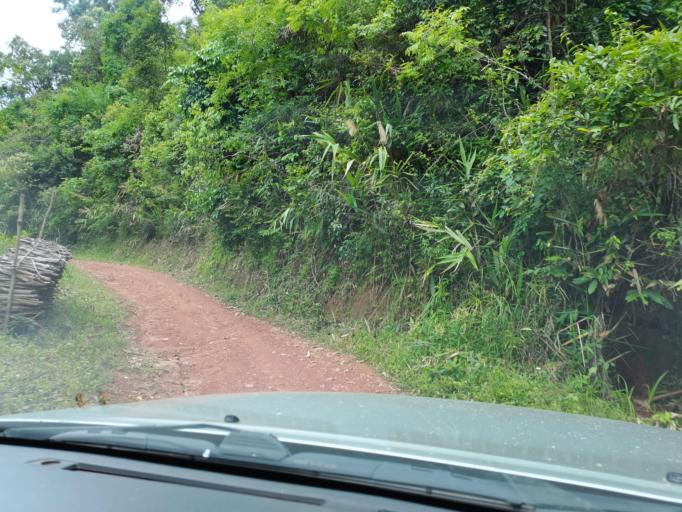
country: LA
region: Loungnamtha
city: Muang Nale
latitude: 20.5094
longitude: 101.0829
